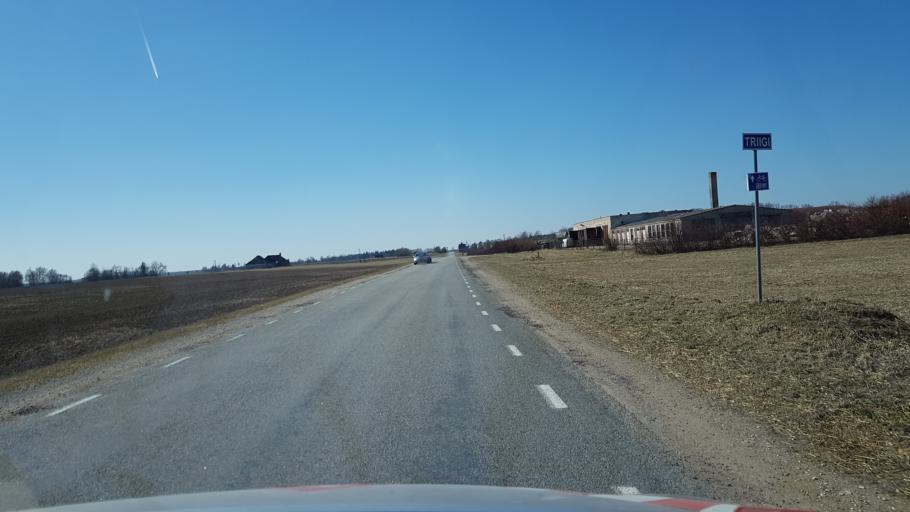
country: EE
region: Laeaene-Virumaa
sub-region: Vaeike-Maarja vald
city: Vaike-Maarja
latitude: 59.1135
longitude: 26.3522
